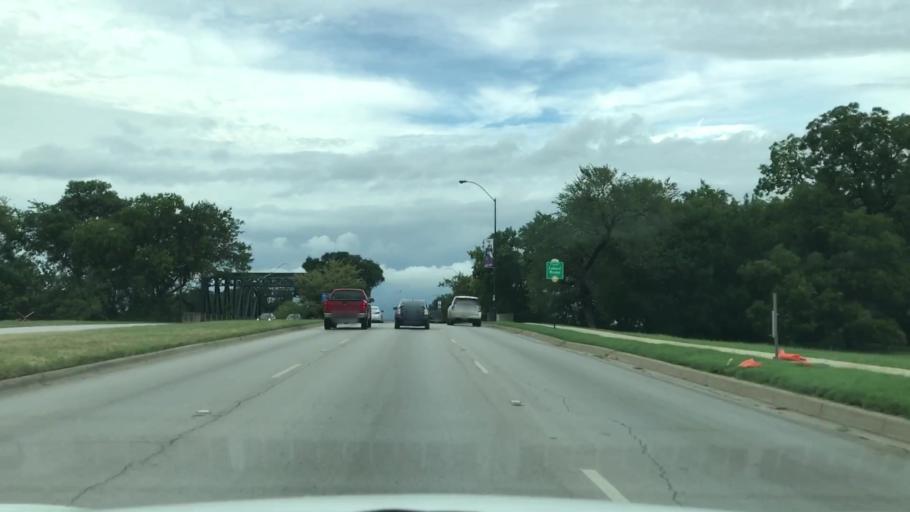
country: US
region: Texas
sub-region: Tarrant County
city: Fort Worth
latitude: 32.7233
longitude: -97.3611
